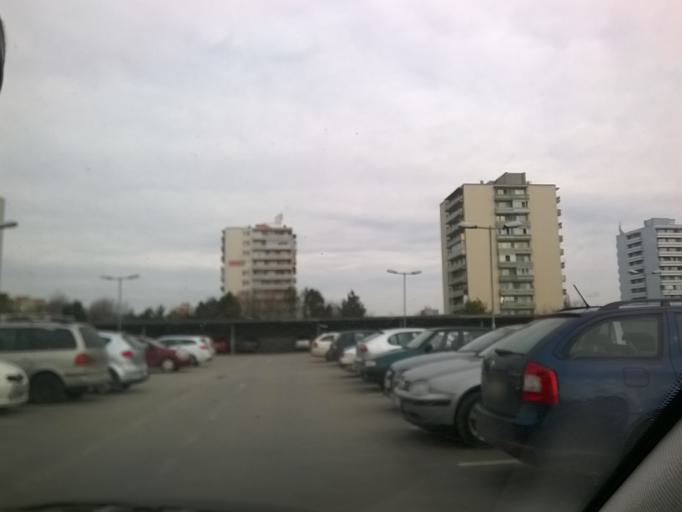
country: SK
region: Nitriansky
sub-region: Okres Nitra
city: Nitra
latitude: 48.3092
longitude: 18.0989
